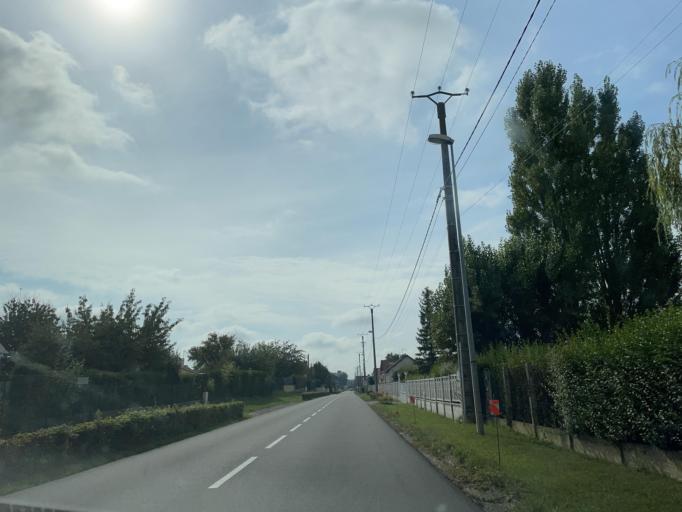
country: FR
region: Ile-de-France
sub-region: Departement de Seine-et-Marne
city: Guerard
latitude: 48.8672
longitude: 2.9909
